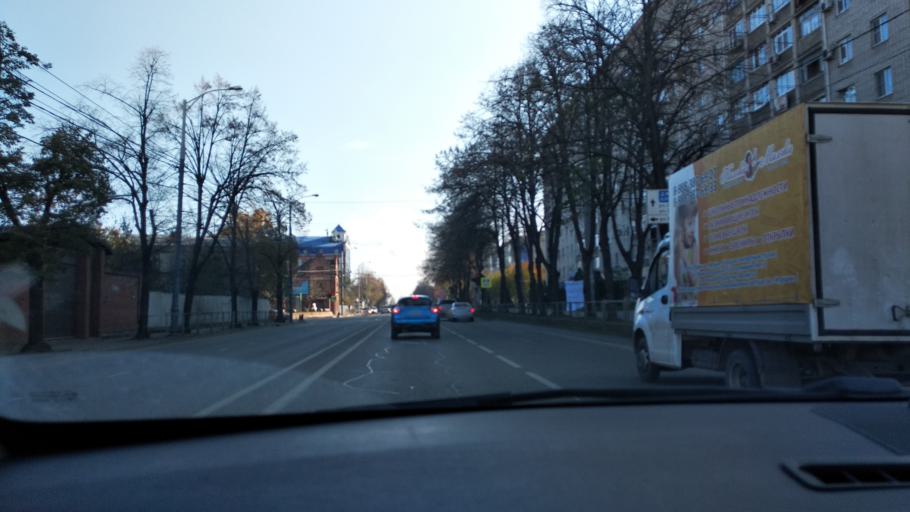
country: RU
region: Krasnodarskiy
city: Krasnodar
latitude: 45.0249
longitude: 39.0374
